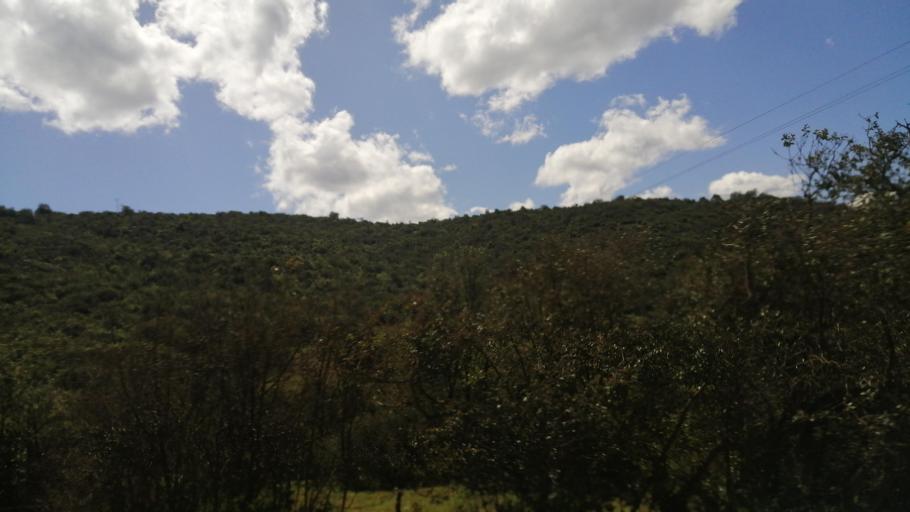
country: CL
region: Valparaiso
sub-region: Provincia de Marga Marga
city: Limache
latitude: -33.2018
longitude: -71.2534
